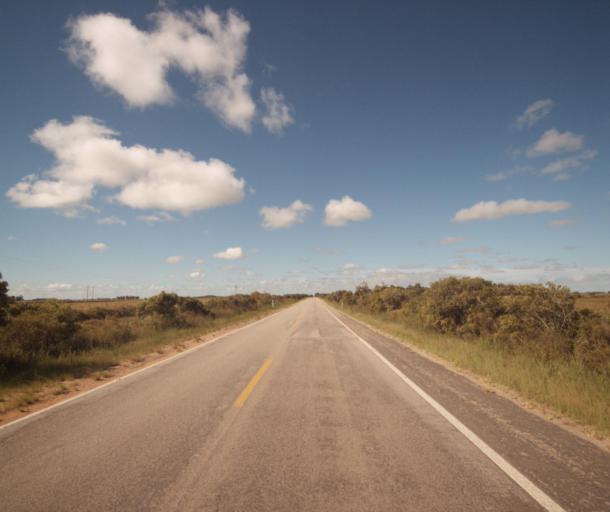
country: BR
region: Rio Grande do Sul
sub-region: Santa Vitoria Do Palmar
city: Santa Vitoria do Palmar
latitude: -33.3794
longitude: -53.1962
